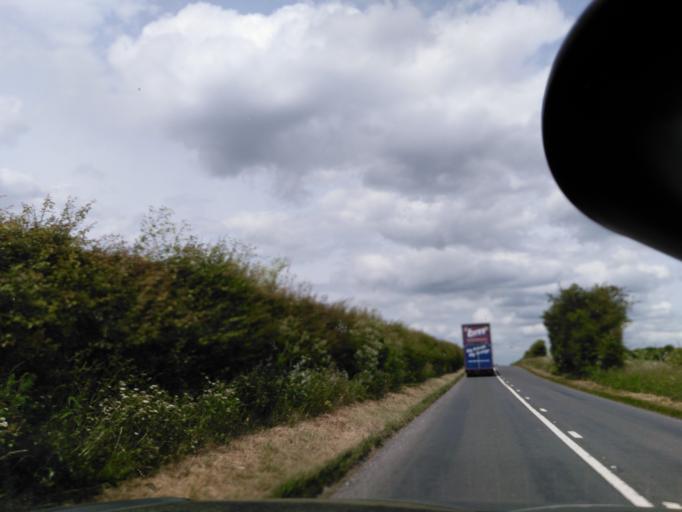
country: GB
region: England
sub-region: Wiltshire
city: Winterbourne Stoke
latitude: 51.1677
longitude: -1.8594
